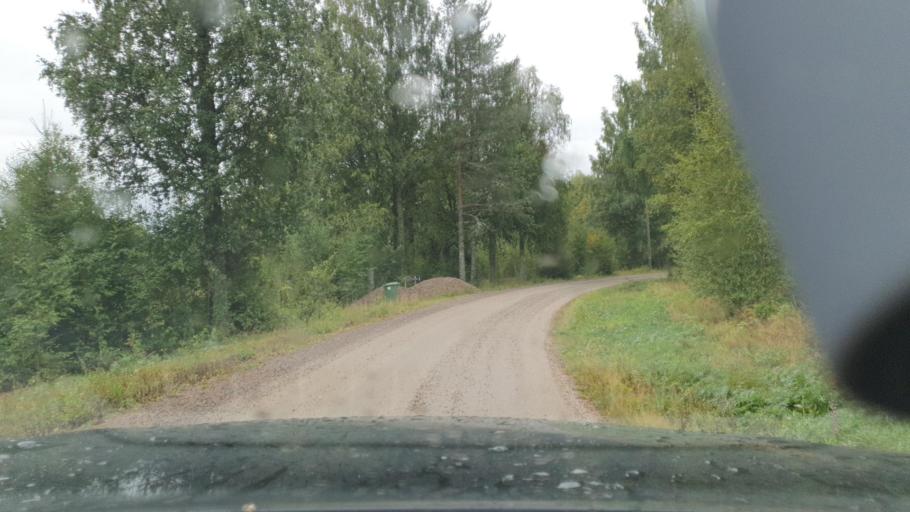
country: NO
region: Hedmark
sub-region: Asnes
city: Flisa
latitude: 60.7730
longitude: 12.4441
